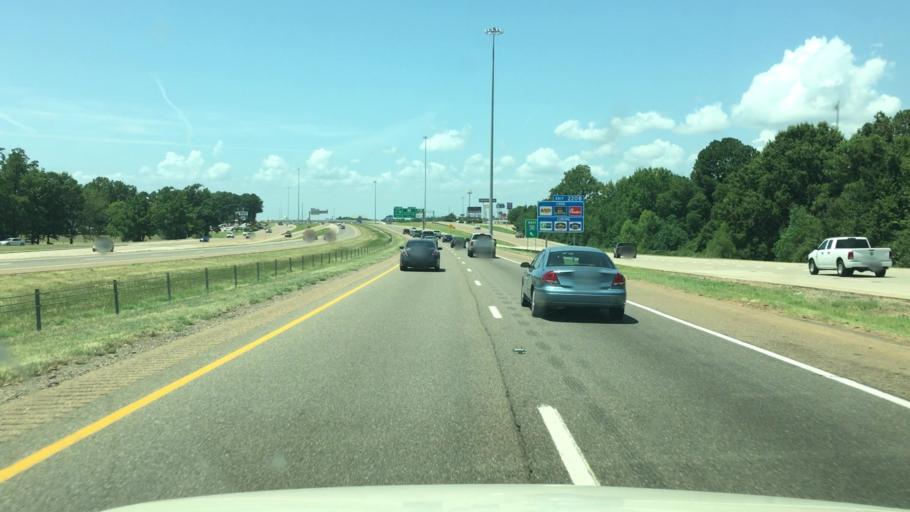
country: US
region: Arkansas
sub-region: Miller County
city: Texarkana
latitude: 33.4692
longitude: -94.0571
